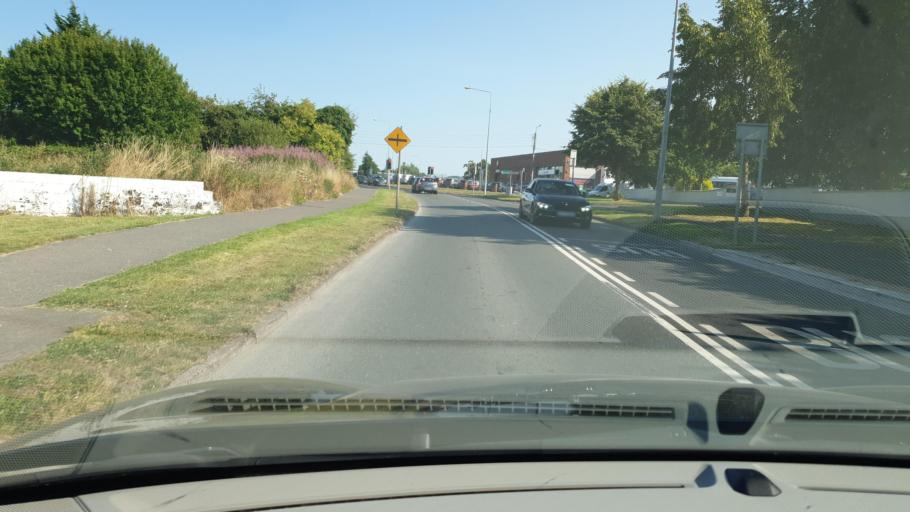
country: IE
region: Leinster
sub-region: An Mhi
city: Navan
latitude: 53.6469
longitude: -6.6995
